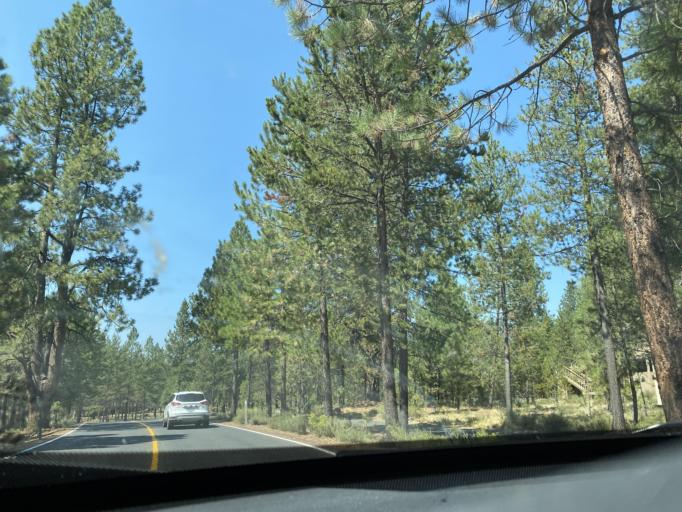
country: US
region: Oregon
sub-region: Deschutes County
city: Sunriver
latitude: 43.8892
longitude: -121.4337
